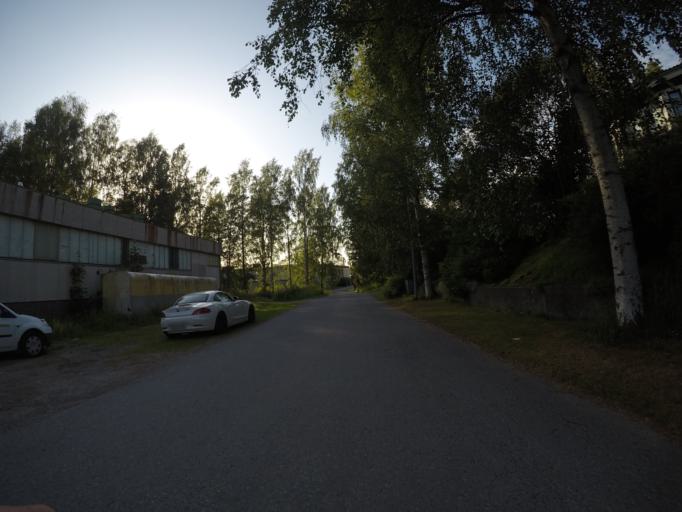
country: FI
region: Haeme
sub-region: Haemeenlinna
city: Haemeenlinna
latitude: 60.9852
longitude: 24.4454
